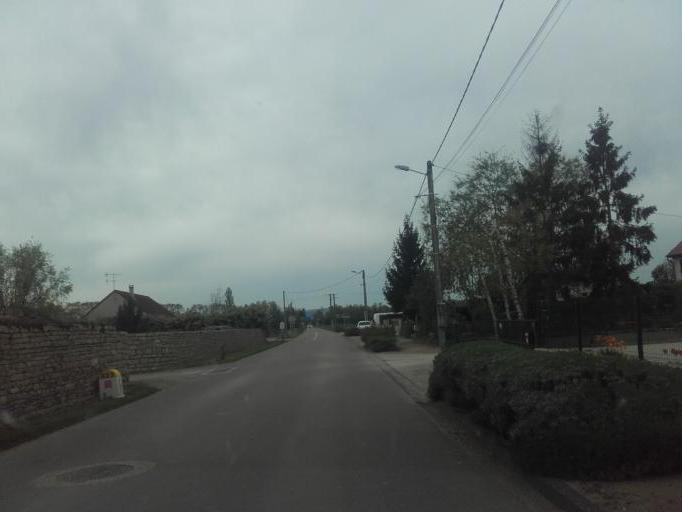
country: FR
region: Bourgogne
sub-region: Departement de Saone-et-Loire
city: Demigny
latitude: 46.9520
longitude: 4.8393
